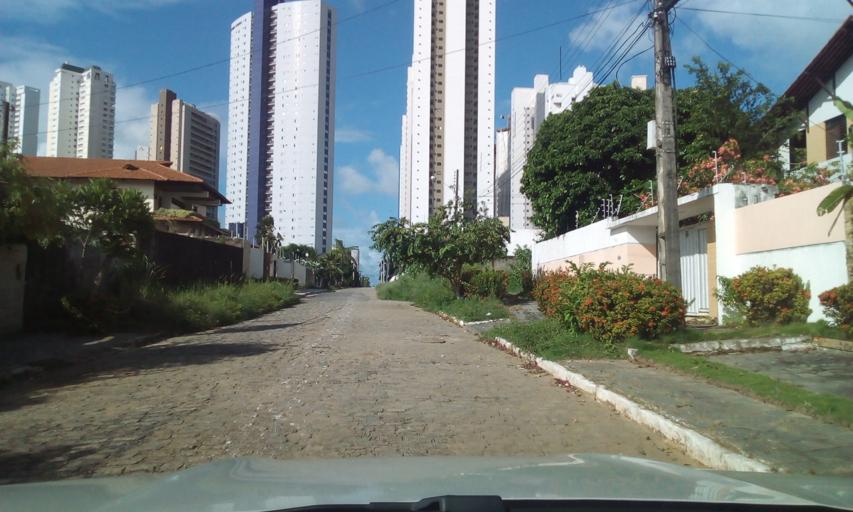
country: BR
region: Paraiba
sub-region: Joao Pessoa
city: Joao Pessoa
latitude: -7.1326
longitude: -34.8319
